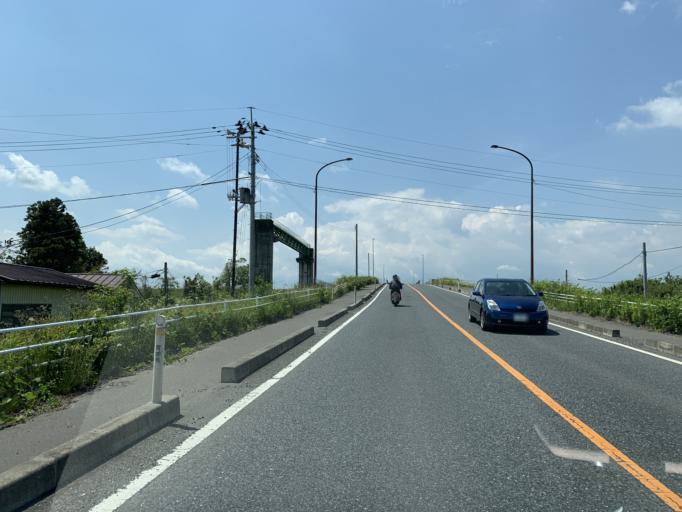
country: JP
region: Miyagi
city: Kogota
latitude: 38.5648
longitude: 141.0463
